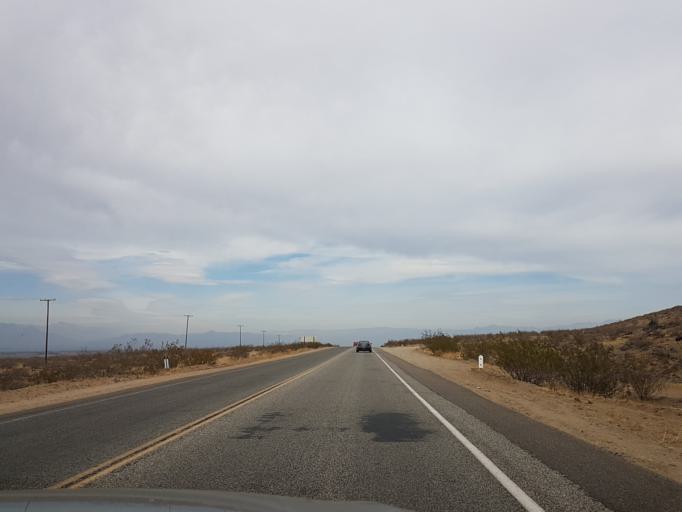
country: US
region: California
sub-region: Kern County
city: Ridgecrest
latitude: 35.5535
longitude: -117.7136
